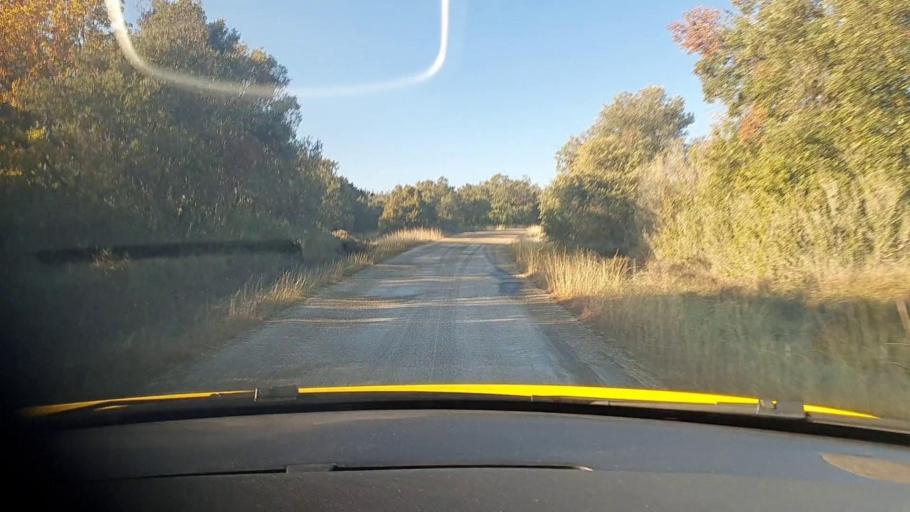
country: FR
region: Languedoc-Roussillon
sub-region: Departement du Gard
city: Goudargues
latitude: 44.1692
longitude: 4.3550
